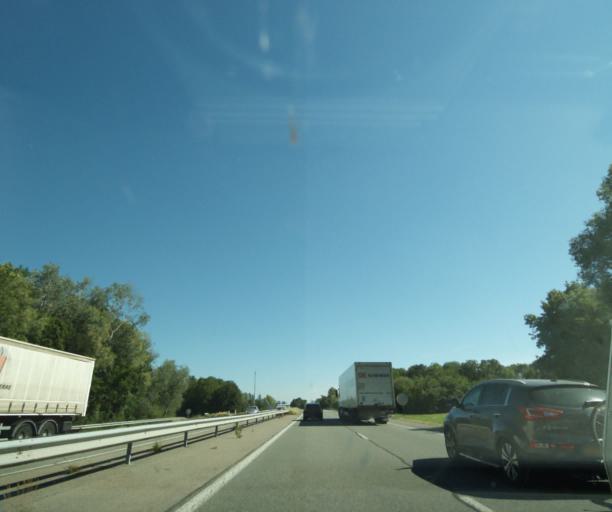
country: FR
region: Champagne-Ardenne
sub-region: Departement de la Haute-Marne
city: Avrecourt
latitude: 47.9927
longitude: 5.5124
